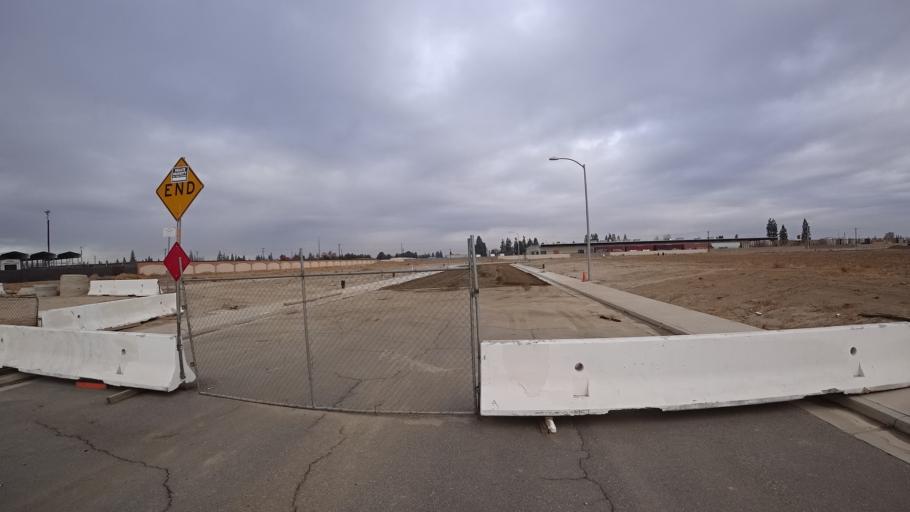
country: US
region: California
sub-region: Kern County
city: Greenfield
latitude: 35.3089
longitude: -119.0693
